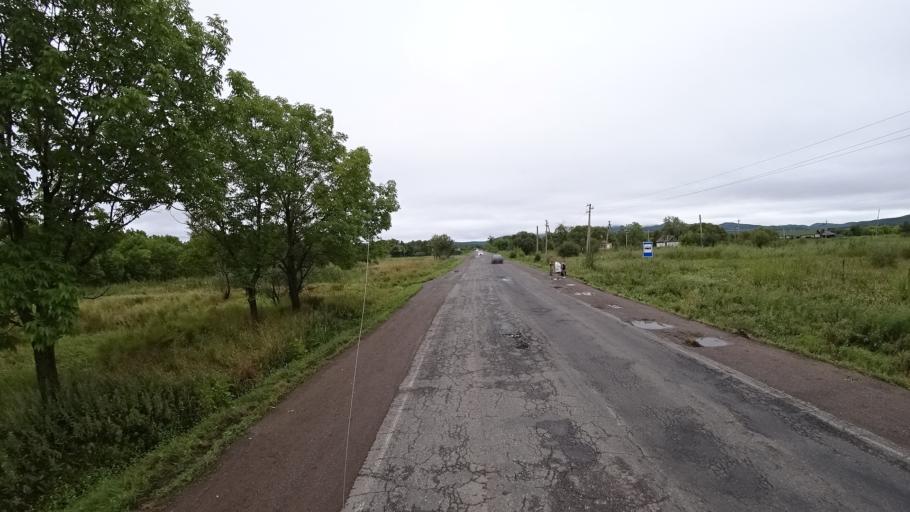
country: RU
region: Primorskiy
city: Monastyrishche
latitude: 44.1956
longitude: 132.4794
